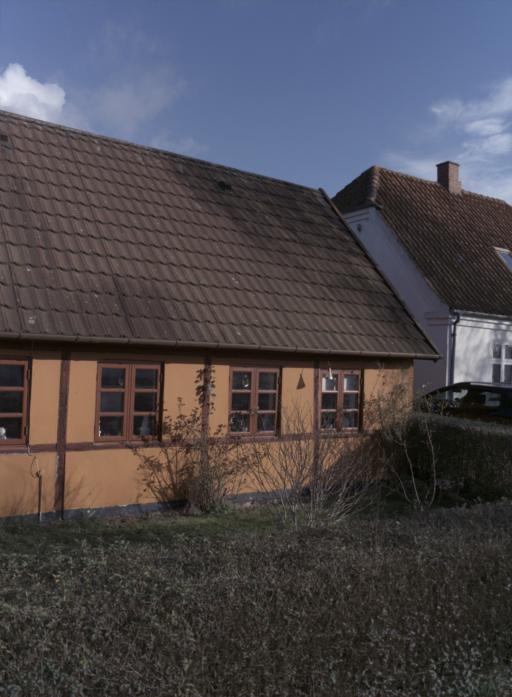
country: DK
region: Zealand
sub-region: Kalundborg Kommune
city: Kalundborg
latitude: 55.6851
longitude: 11.1351
